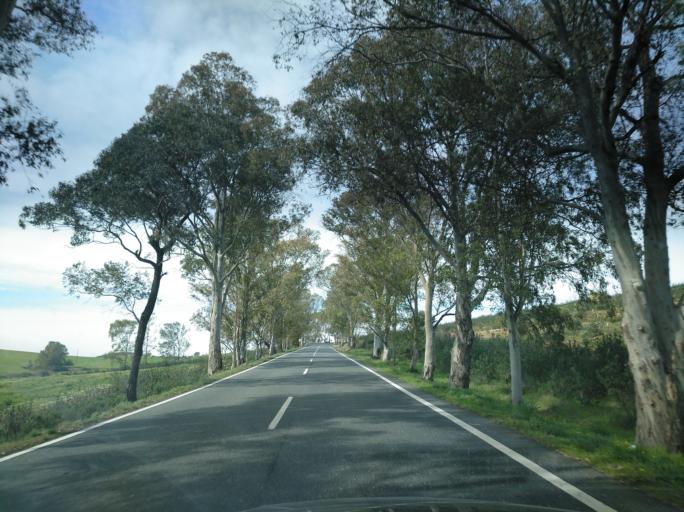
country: PT
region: Beja
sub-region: Mertola
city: Mertola
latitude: 37.7063
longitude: -7.7510
